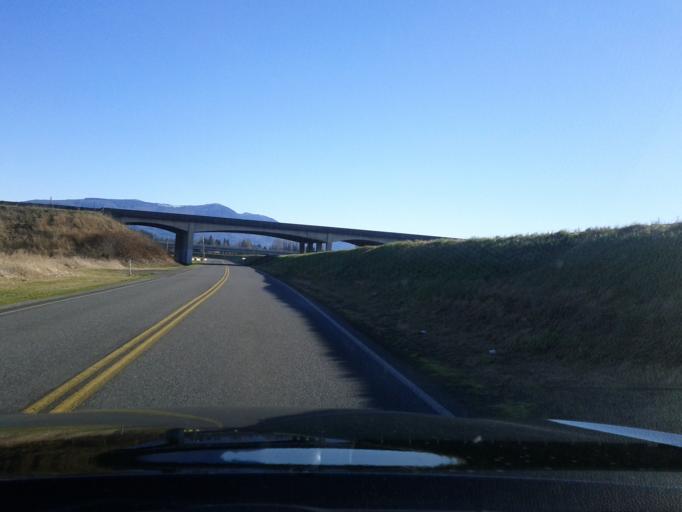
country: US
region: Washington
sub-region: Skagit County
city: Mount Vernon
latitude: 48.4463
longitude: -122.3430
